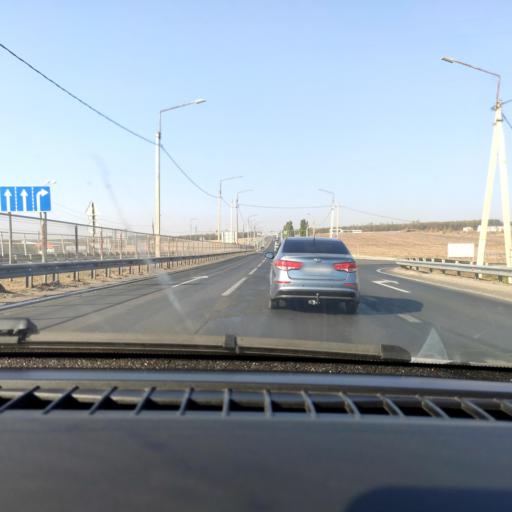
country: RU
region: Voronezj
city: Pridonskoy
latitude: 51.6509
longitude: 39.0643
